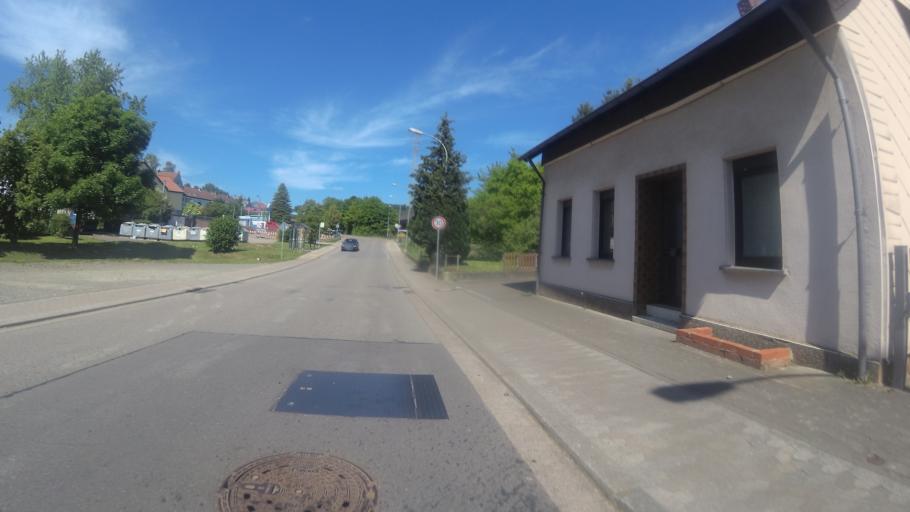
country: DE
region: Saarland
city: Quierschied
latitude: 49.3288
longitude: 7.0562
